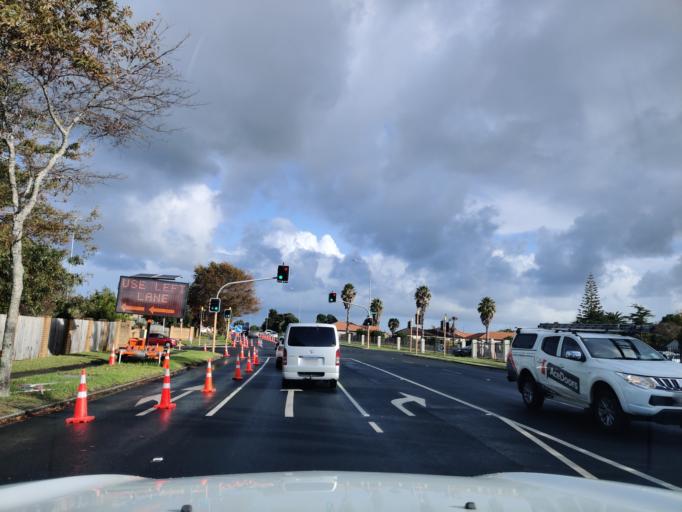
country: NZ
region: Auckland
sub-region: Auckland
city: Pakuranga
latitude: -36.9192
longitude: 174.9131
